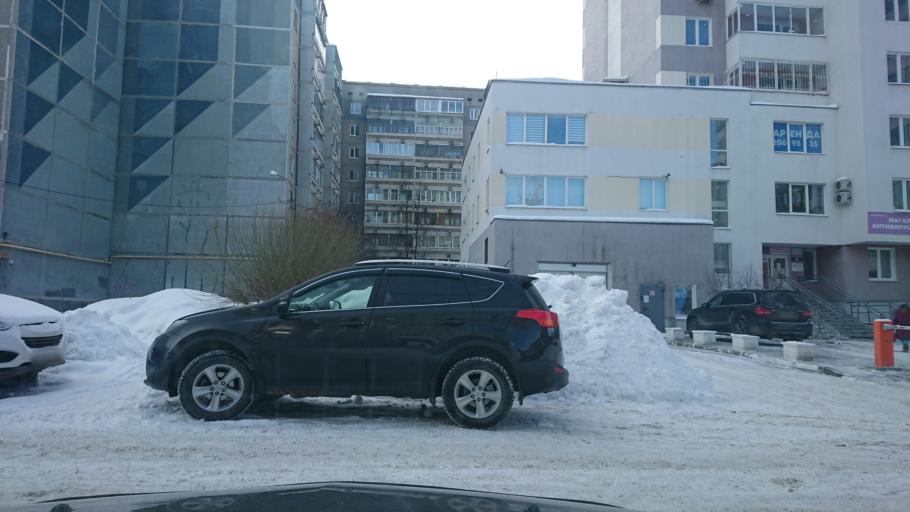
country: RU
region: Sverdlovsk
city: Sovkhoznyy
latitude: 56.7988
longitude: 60.5896
